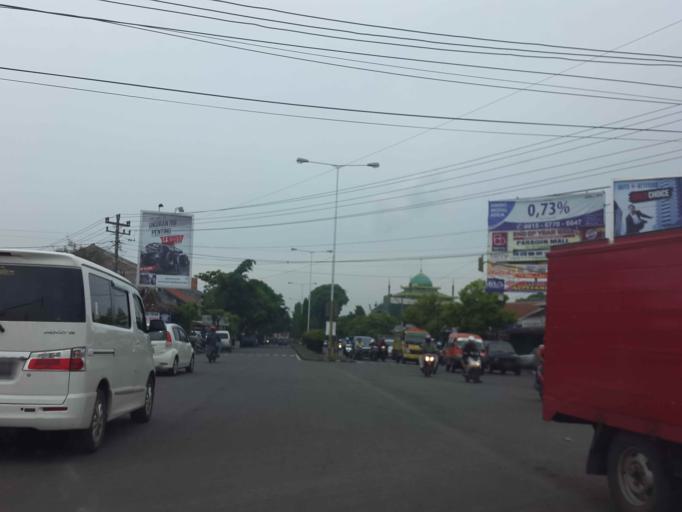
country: ID
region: Central Java
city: Semarang
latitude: -6.9911
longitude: 110.4581
